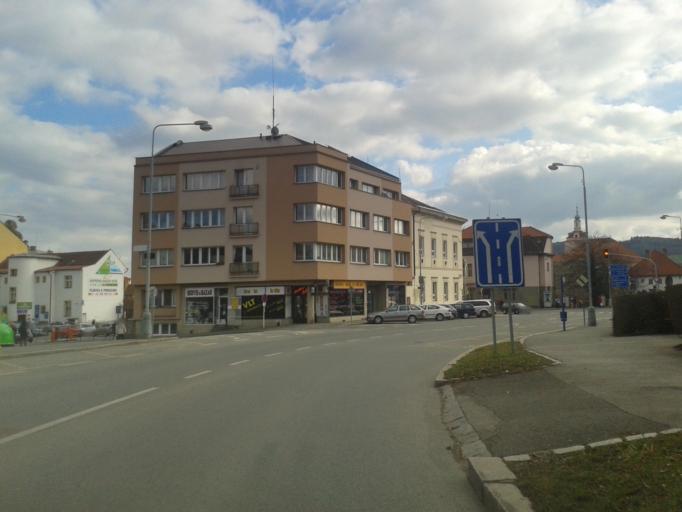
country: CZ
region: Central Bohemia
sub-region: Okres Beroun
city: Beroun
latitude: 49.9657
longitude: 14.0702
